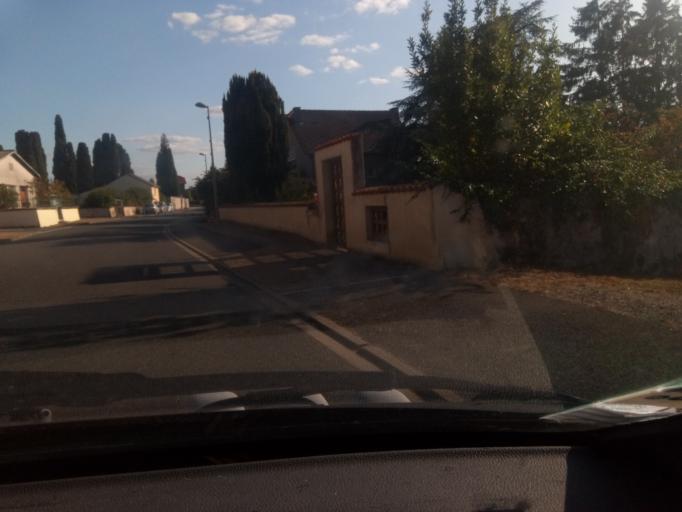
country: FR
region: Poitou-Charentes
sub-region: Departement de la Vienne
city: Lussac-les-Chateaux
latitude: 46.3418
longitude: 0.7058
